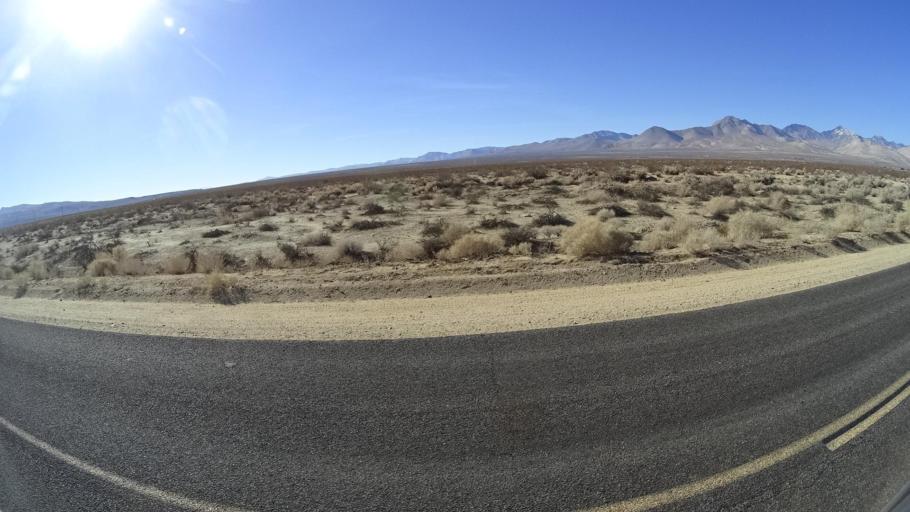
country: US
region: California
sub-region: Kern County
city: Inyokern
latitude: 35.6112
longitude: -117.8018
